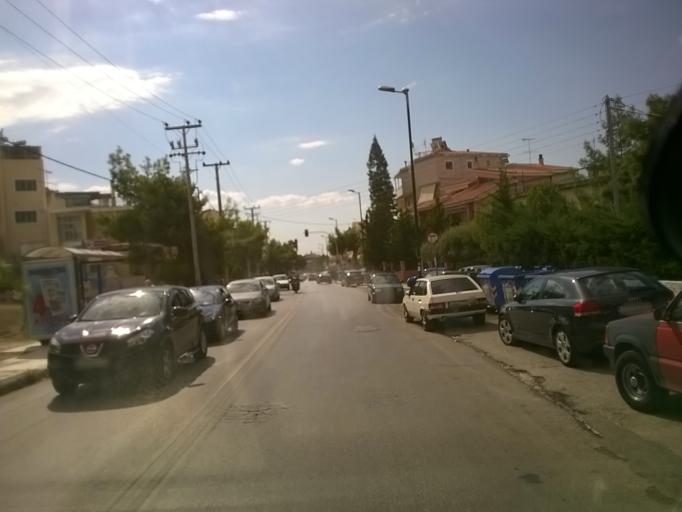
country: GR
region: Attica
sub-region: Nomarchia Athinas
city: Glyfada
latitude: 37.8845
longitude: 23.7623
